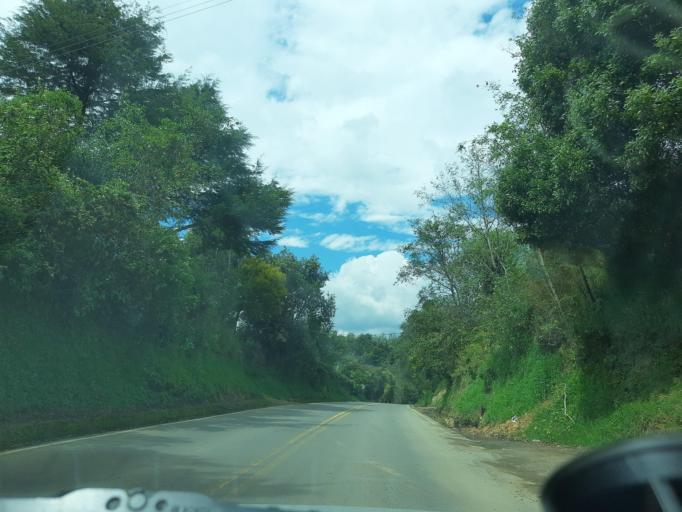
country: CO
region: Boyaca
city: Chiquinquira
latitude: 5.6204
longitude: -73.7495
